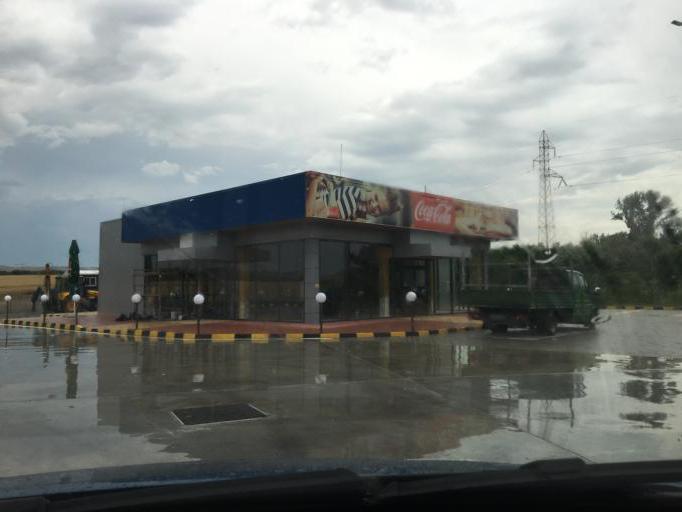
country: BG
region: Sliven
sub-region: Obshtina Nova Zagora
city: Nova Zagora
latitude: 42.4529
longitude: 26.0516
